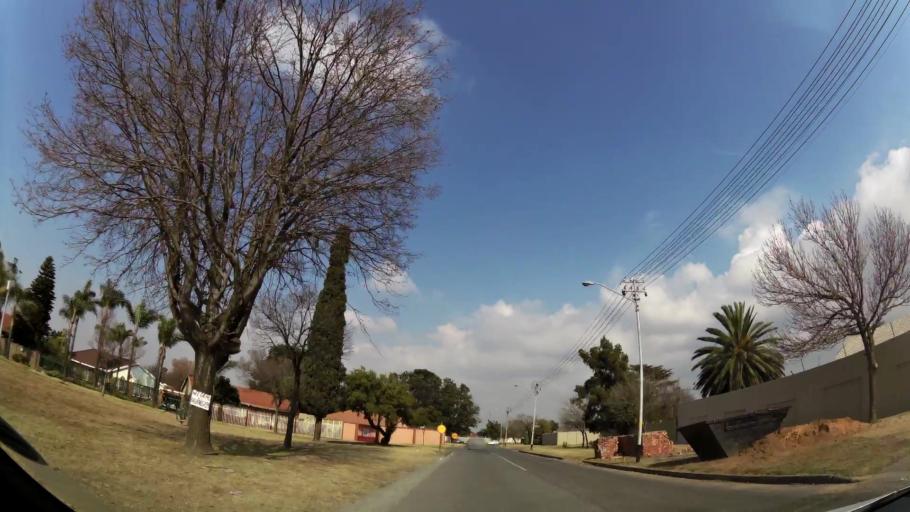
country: ZA
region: Gauteng
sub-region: Ekurhuleni Metropolitan Municipality
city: Germiston
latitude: -26.1750
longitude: 28.1937
